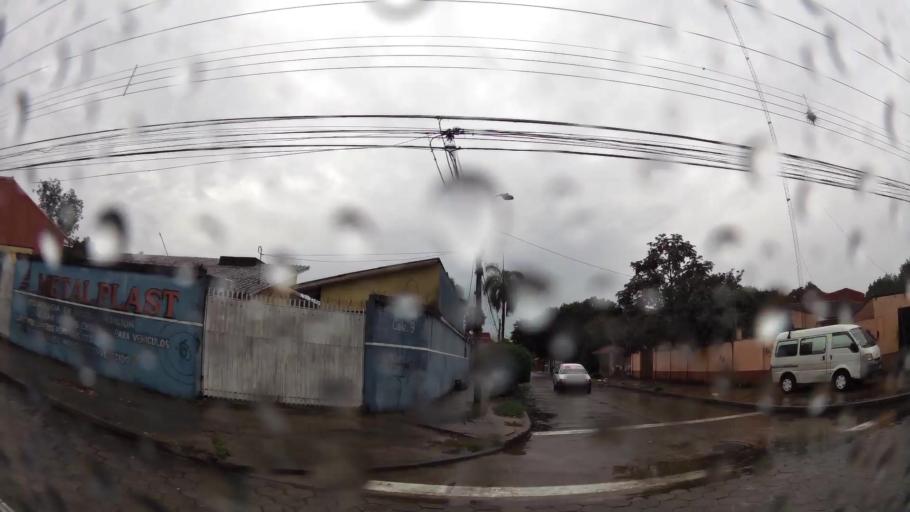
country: BO
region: Santa Cruz
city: Santa Cruz de la Sierra
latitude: -17.7913
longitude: -63.2134
